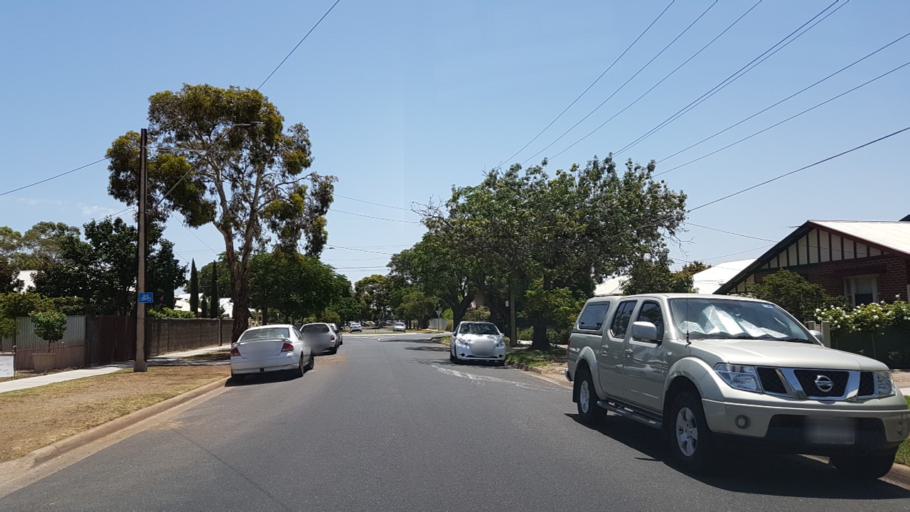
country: AU
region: South Australia
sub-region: Charles Sturt
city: Allenby Gardens
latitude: -34.8951
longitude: 138.5532
